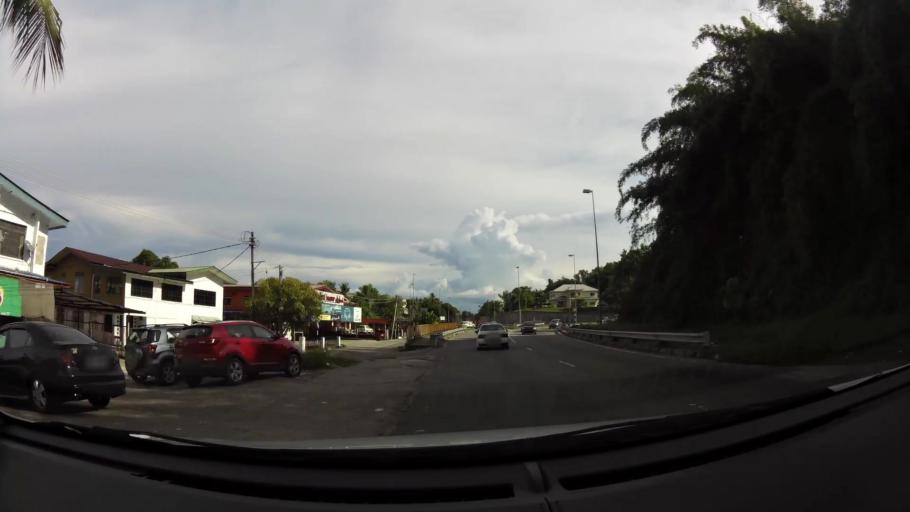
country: BN
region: Brunei and Muara
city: Bandar Seri Begawan
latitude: 4.9716
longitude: 115.0210
